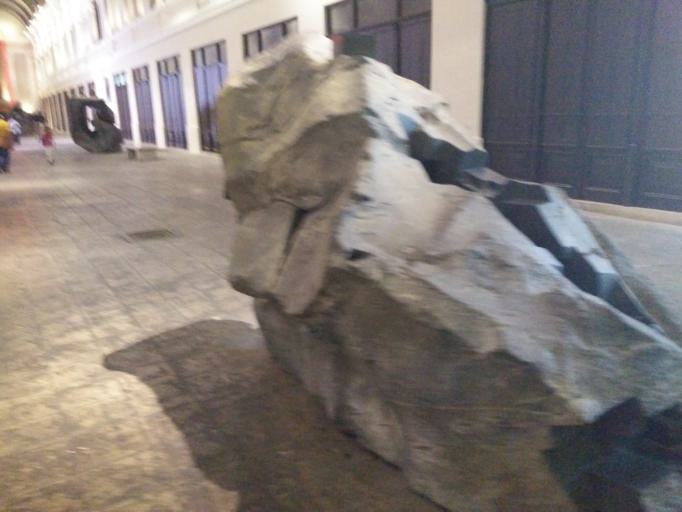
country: MX
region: Yucatan
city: Merida
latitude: 20.9670
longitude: -89.6227
